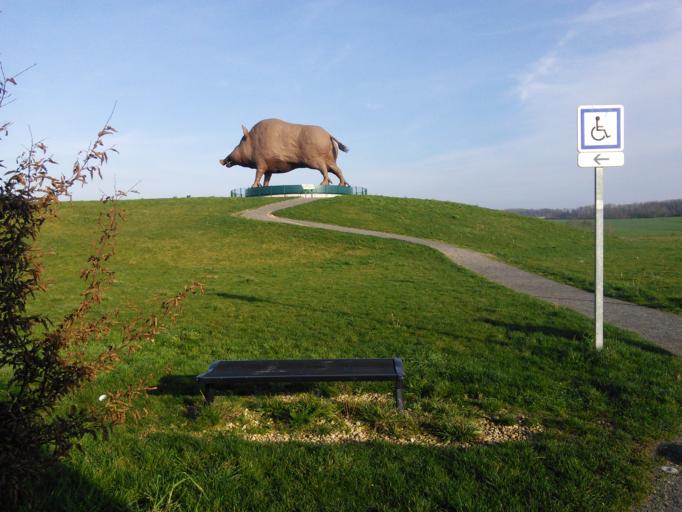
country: FR
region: Champagne-Ardenne
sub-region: Departement des Ardennes
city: Attigny
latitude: 49.5941
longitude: 4.5034
